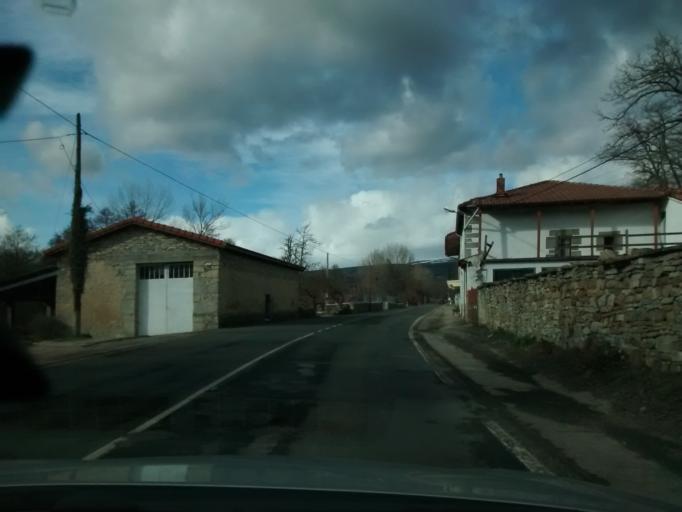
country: ES
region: Castille and Leon
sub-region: Provincia de Burgos
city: Espinosa de los Monteros
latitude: 43.0625
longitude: -3.4979
